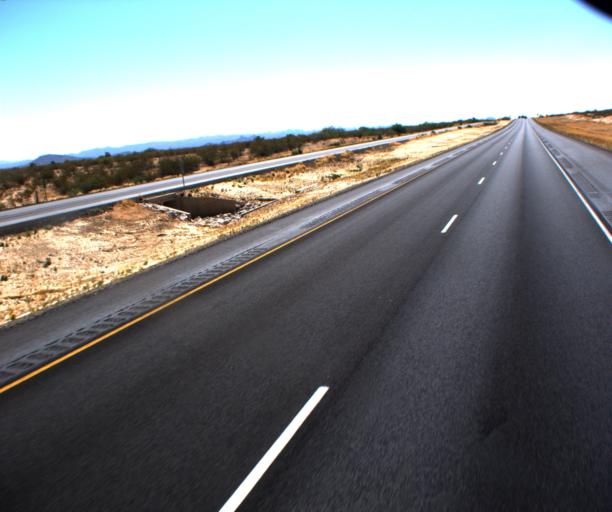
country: US
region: Arizona
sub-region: Yavapai County
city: Congress
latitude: 34.0613
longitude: -112.8619
